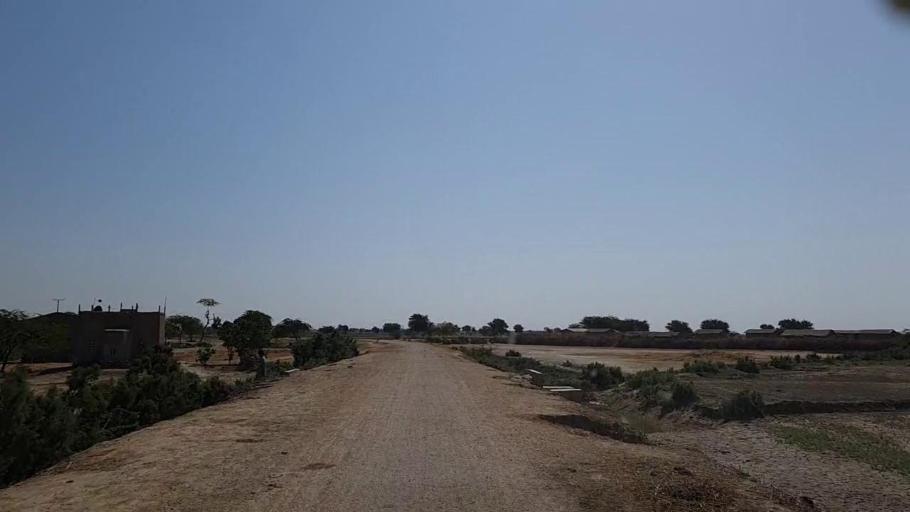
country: PK
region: Sindh
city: Mirpur Batoro
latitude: 24.6787
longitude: 68.3028
